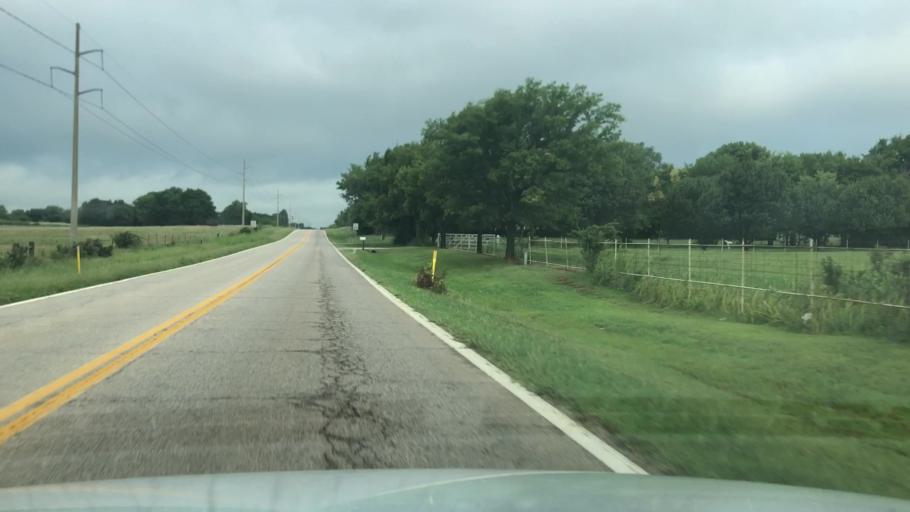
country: US
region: Oklahoma
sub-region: Nowata County
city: Nowata
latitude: 36.7136
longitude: -95.6703
